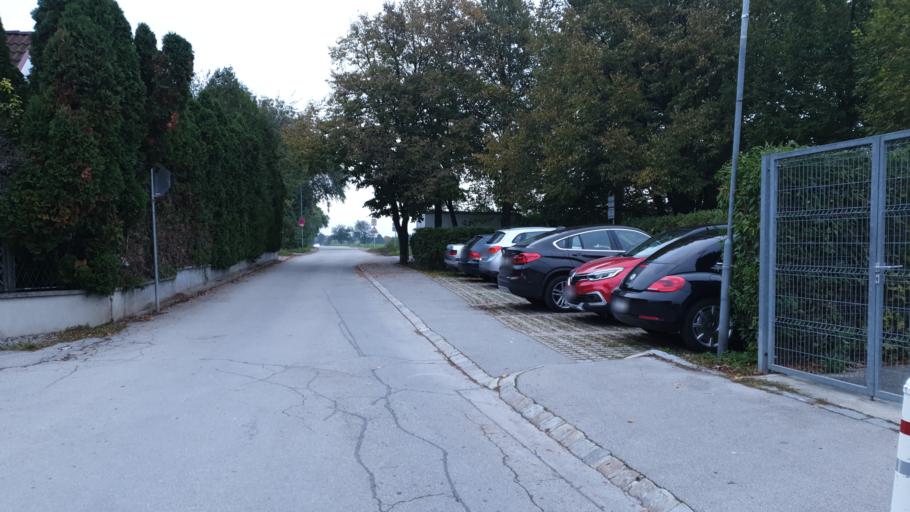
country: AT
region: Lower Austria
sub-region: Politischer Bezirk Wien-Umgebung
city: Gerasdorf bei Wien
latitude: 48.2968
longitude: 16.4583
